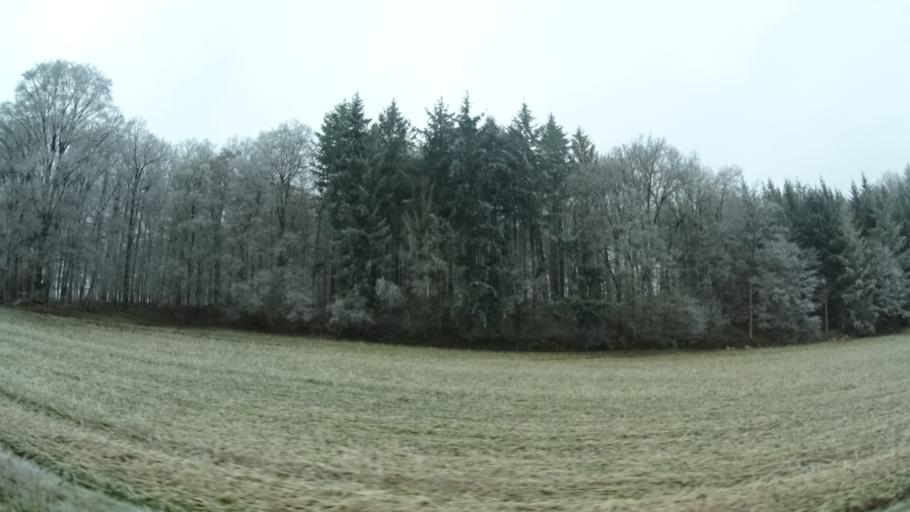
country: DE
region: Baden-Wuerttemberg
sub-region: Regierungsbezirk Stuttgart
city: Igersheim
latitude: 49.5475
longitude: 9.8221
